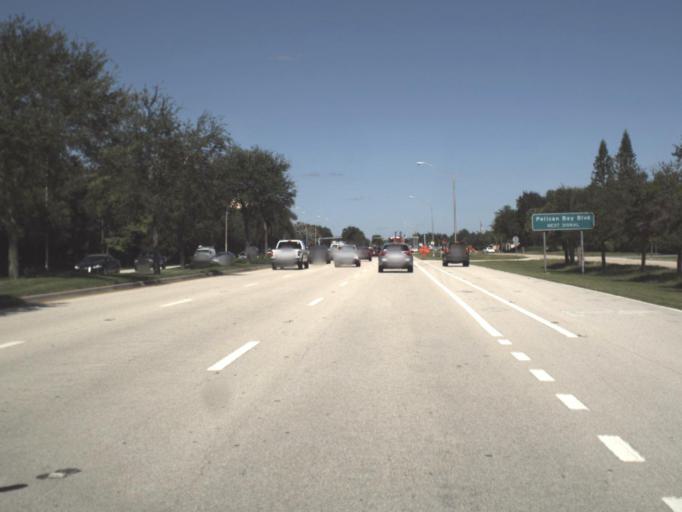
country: US
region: Florida
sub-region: Collier County
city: Pelican Bay
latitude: 26.2414
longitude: -81.8009
